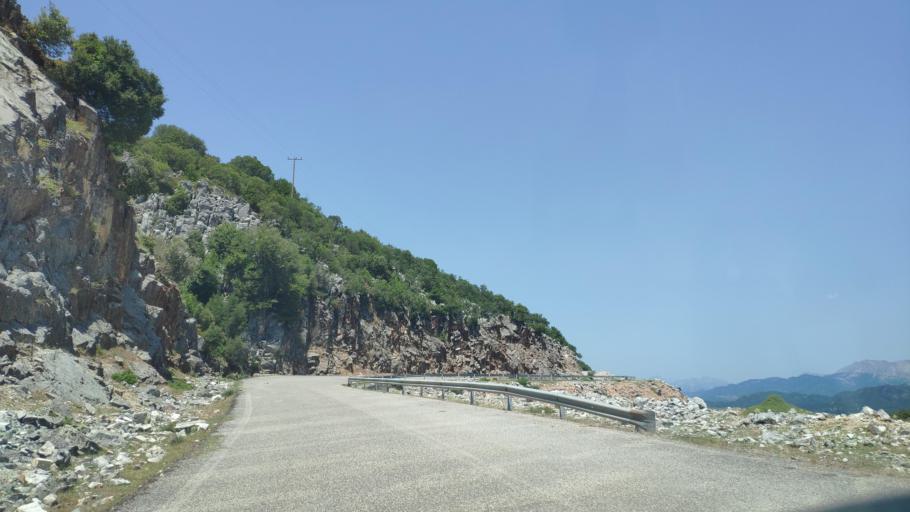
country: GR
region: Thessaly
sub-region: Nomos Kardhitsas
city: Anthiro
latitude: 39.1216
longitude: 21.4014
